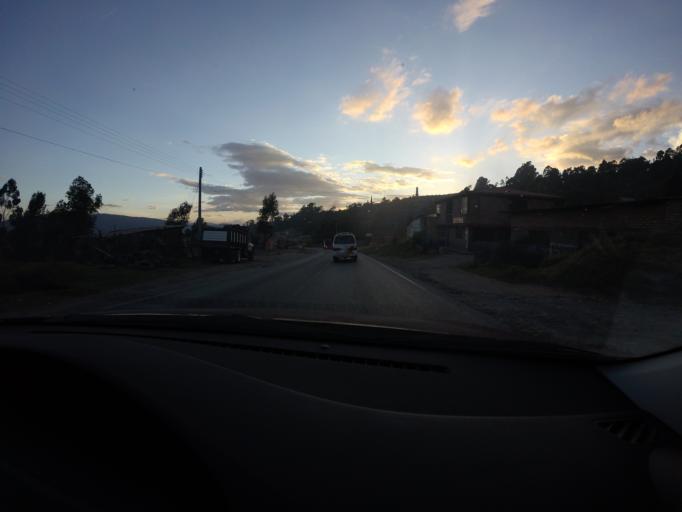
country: CO
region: Cundinamarca
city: Nemocon
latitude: 5.1333
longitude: -73.9039
